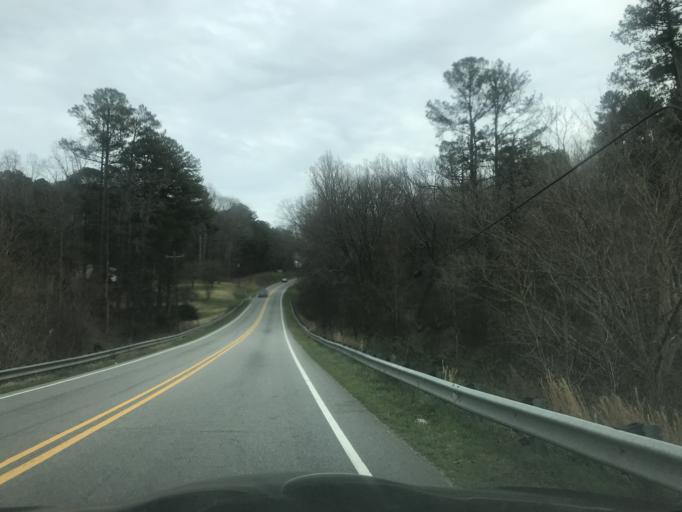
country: US
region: North Carolina
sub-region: Franklin County
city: Franklinton
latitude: 36.1072
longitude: -78.4718
